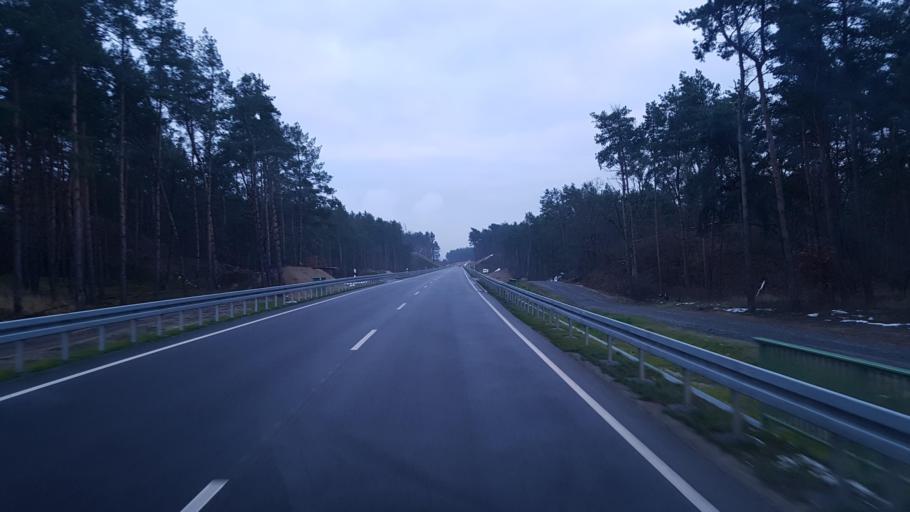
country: DE
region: Brandenburg
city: Wildau
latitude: 52.3217
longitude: 13.6573
